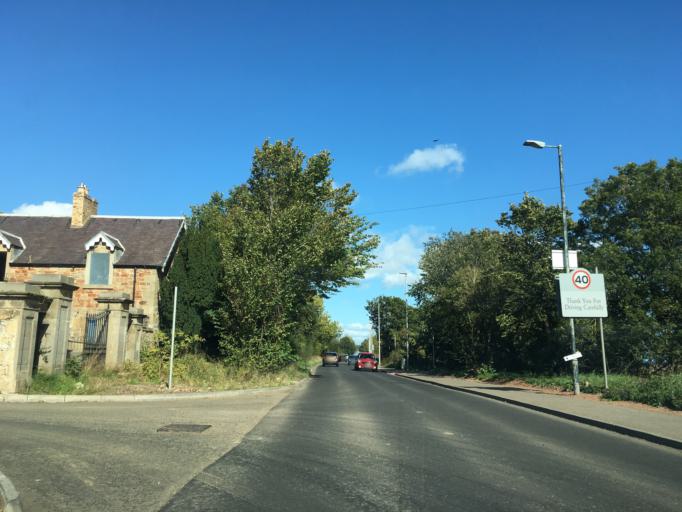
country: GB
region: Scotland
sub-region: Midlothian
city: Bonnyrigg
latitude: 55.9178
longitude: -3.1156
